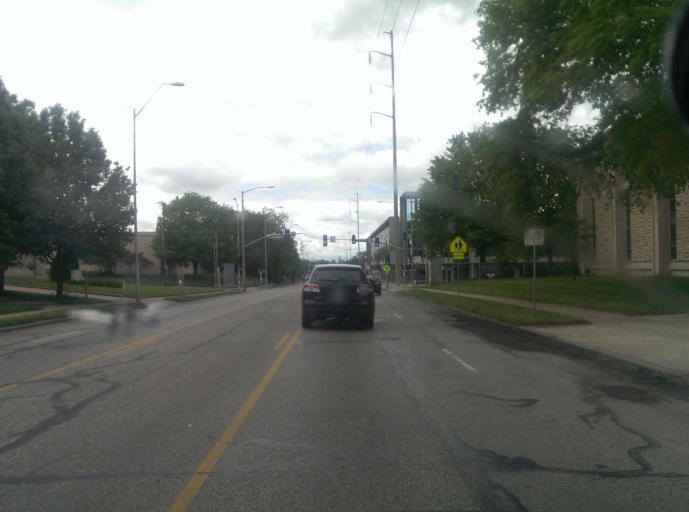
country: US
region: Kansas
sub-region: Johnson County
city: Westwood
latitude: 39.0317
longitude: -94.5735
